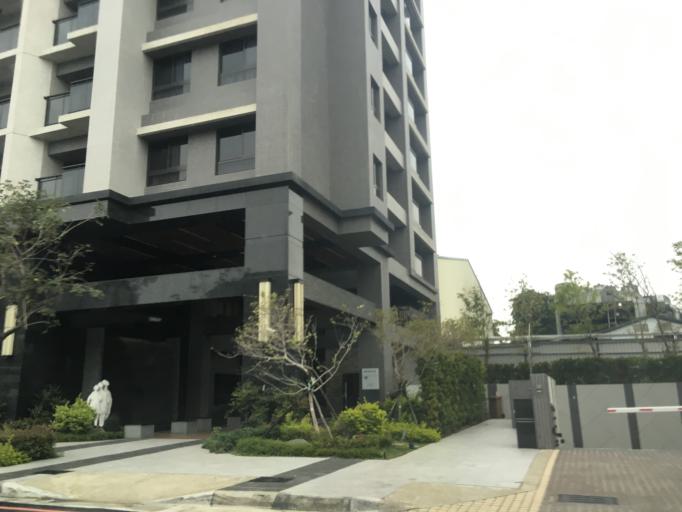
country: TW
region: Taiwan
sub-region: Taichung City
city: Taichung
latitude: 24.1655
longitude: 120.7073
